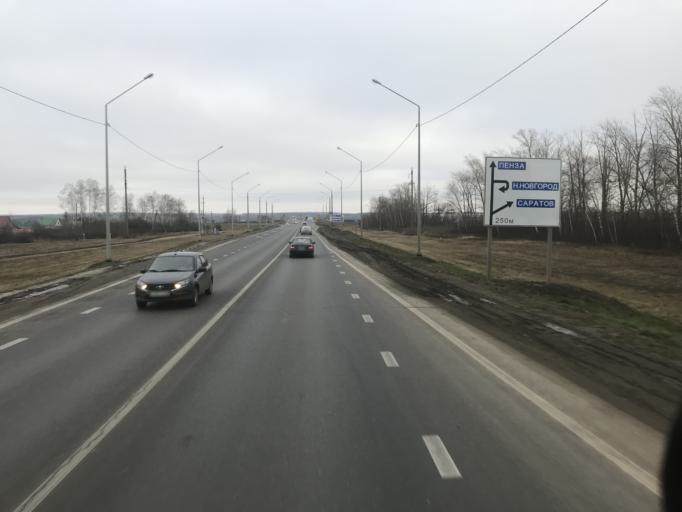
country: RU
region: Penza
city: Bogoslovka
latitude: 53.1308
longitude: 44.7702
